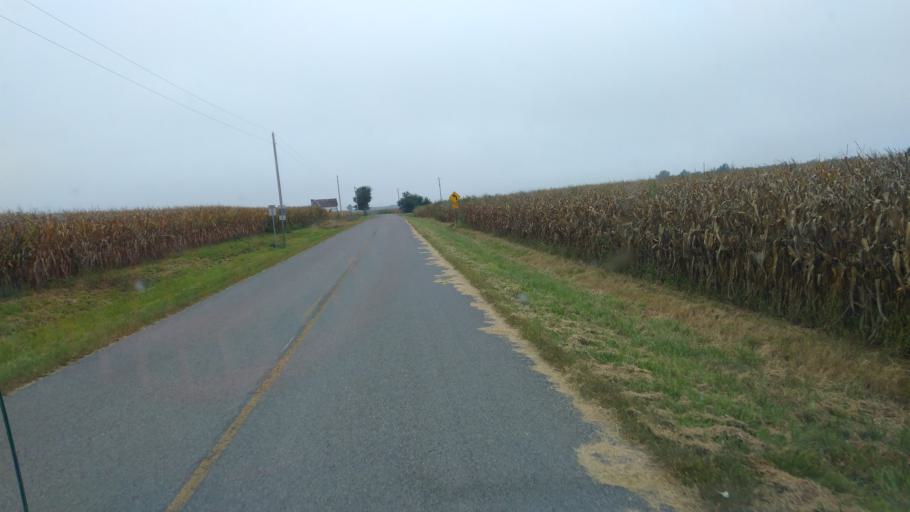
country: US
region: Ohio
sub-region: Logan County
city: Northwood
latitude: 40.4793
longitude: -83.5785
